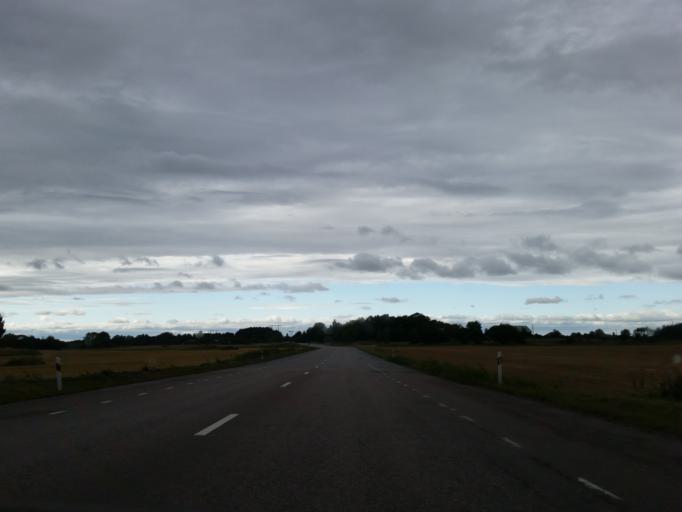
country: SE
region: Uppsala
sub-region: Enkopings Kommun
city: Orsundsbro
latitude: 59.6568
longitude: 17.3461
